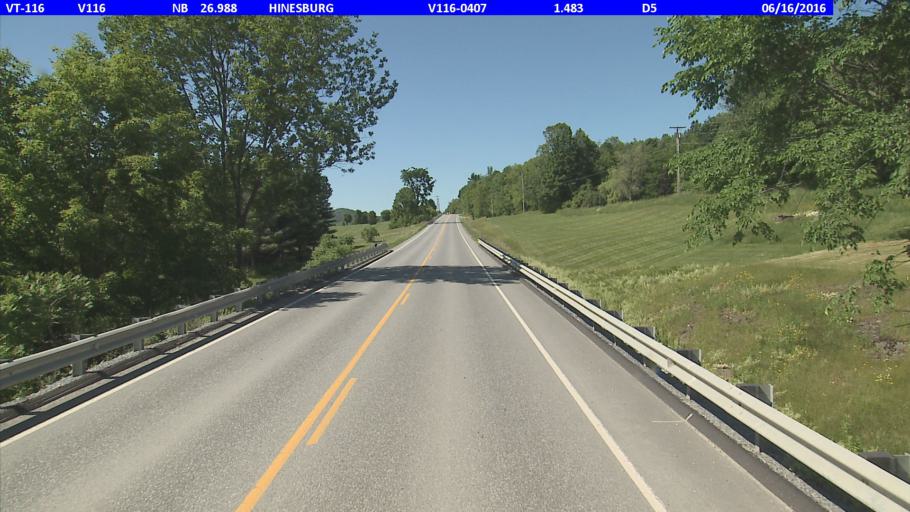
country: US
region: Vermont
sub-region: Chittenden County
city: Hinesburg
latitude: 44.3009
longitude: -73.0741
